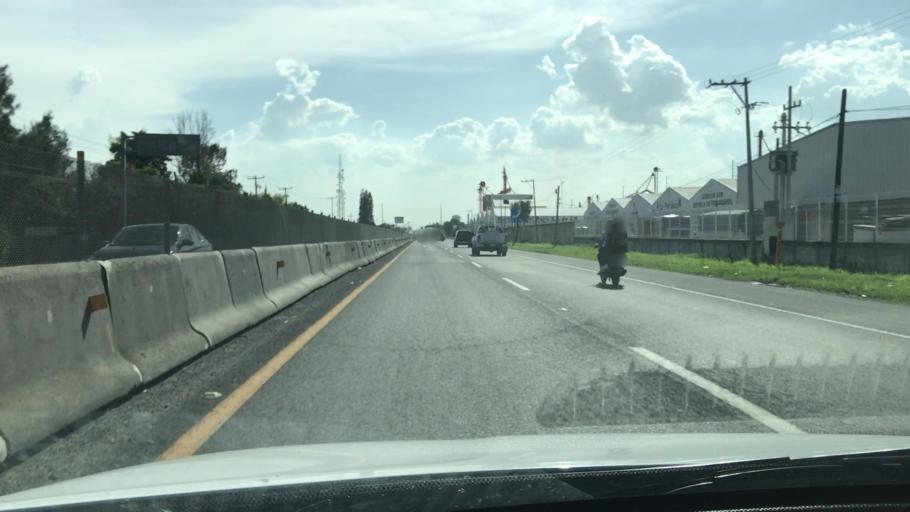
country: MX
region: Guanajuato
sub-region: Cortazar
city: Colonia la Calzada (La Olla)
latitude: 20.5118
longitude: -100.9459
